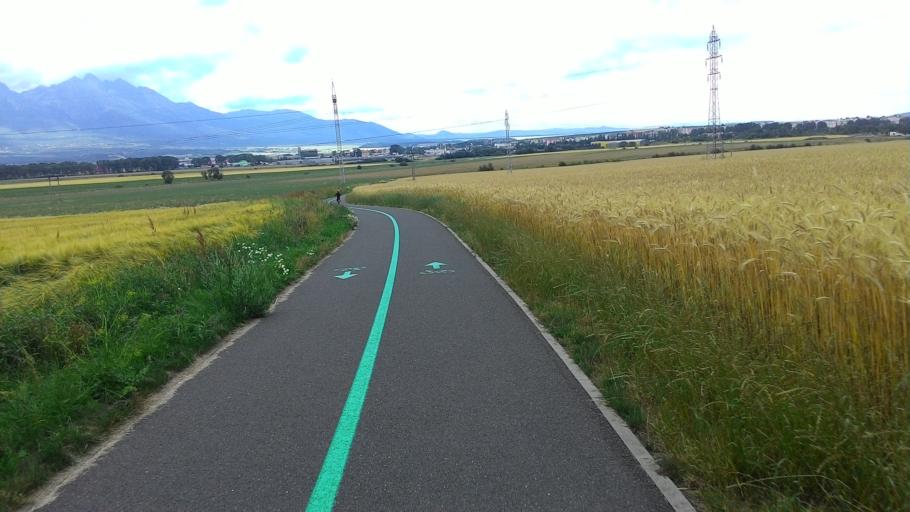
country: SK
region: Presovsky
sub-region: Okres Poprad
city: Poprad
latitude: 49.0400
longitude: 20.2713
